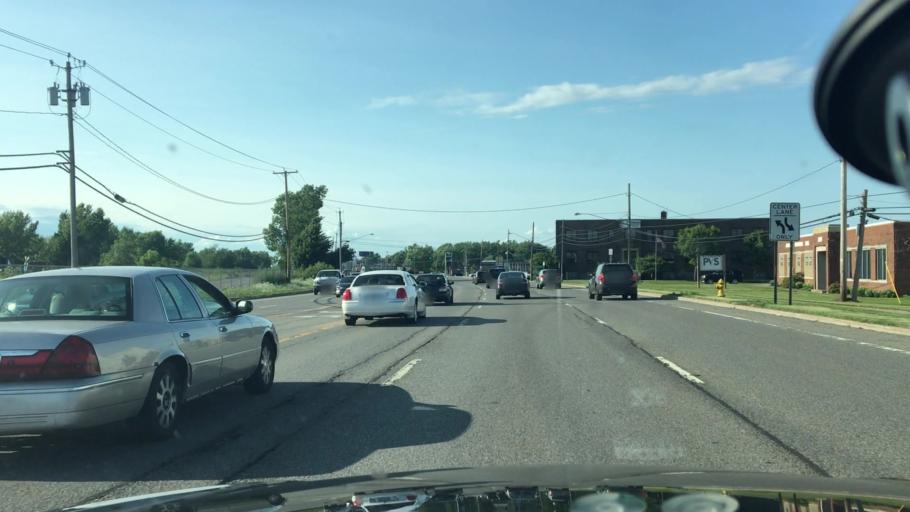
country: US
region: New York
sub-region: Erie County
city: Lackawanna
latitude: 42.8137
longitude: -78.8454
